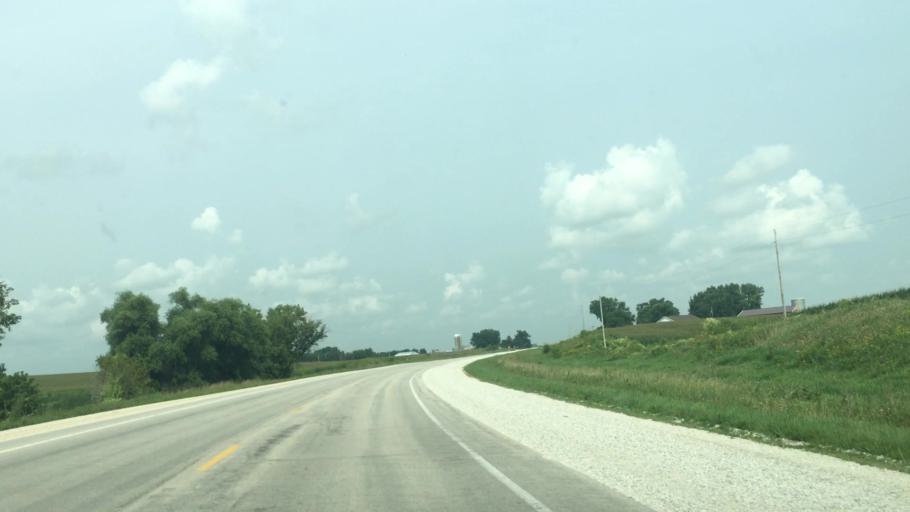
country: US
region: Iowa
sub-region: Winneshiek County
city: Decorah
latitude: 43.4061
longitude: -91.8537
